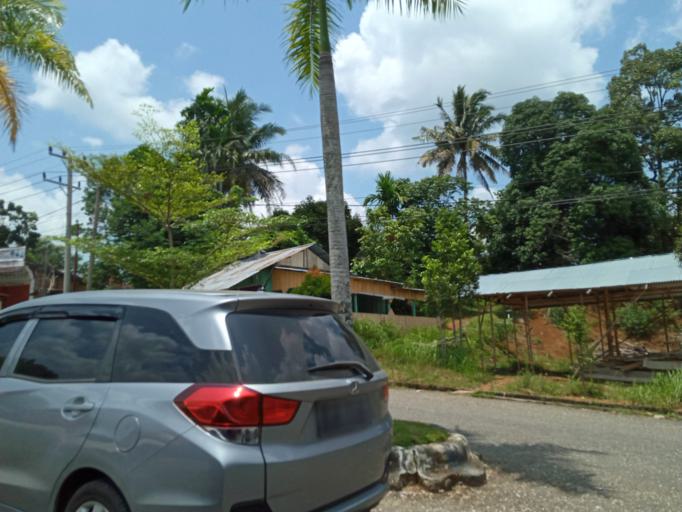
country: ID
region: Jambi
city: Bangko
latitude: -2.0547
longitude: 102.2814
